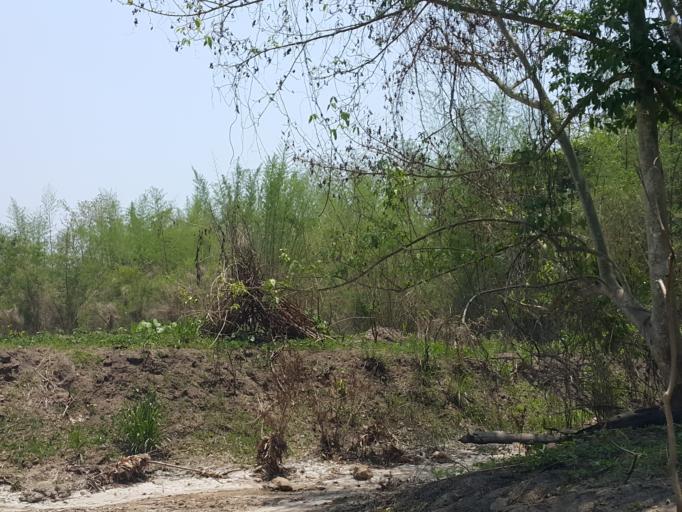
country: TH
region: Kanchanaburi
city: Sai Yok
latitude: 14.2263
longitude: 98.8824
